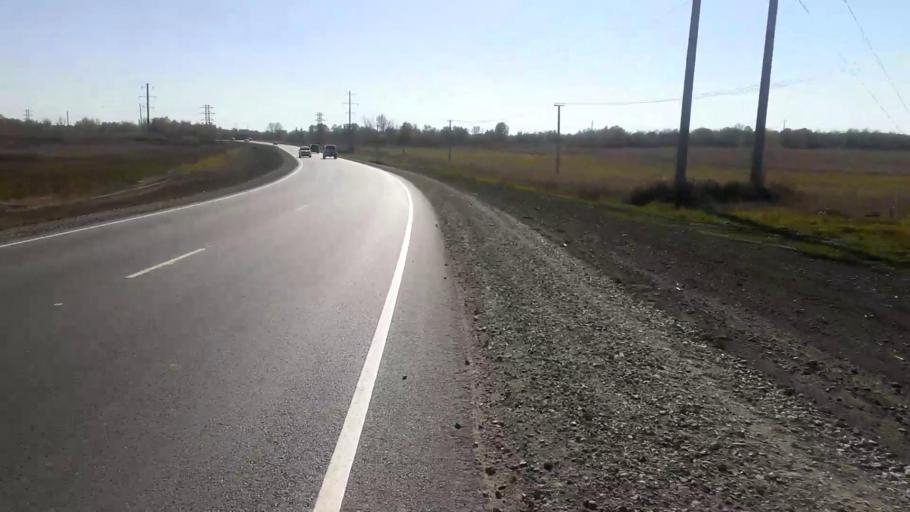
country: RU
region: Altai Krai
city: Sannikovo
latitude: 53.3332
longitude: 83.9379
